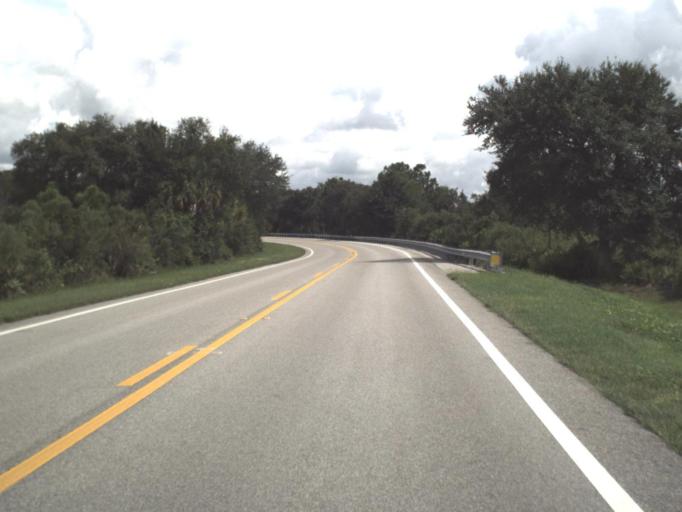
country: US
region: Florida
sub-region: Sarasota County
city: Warm Mineral Springs
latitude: 27.1962
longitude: -82.2235
